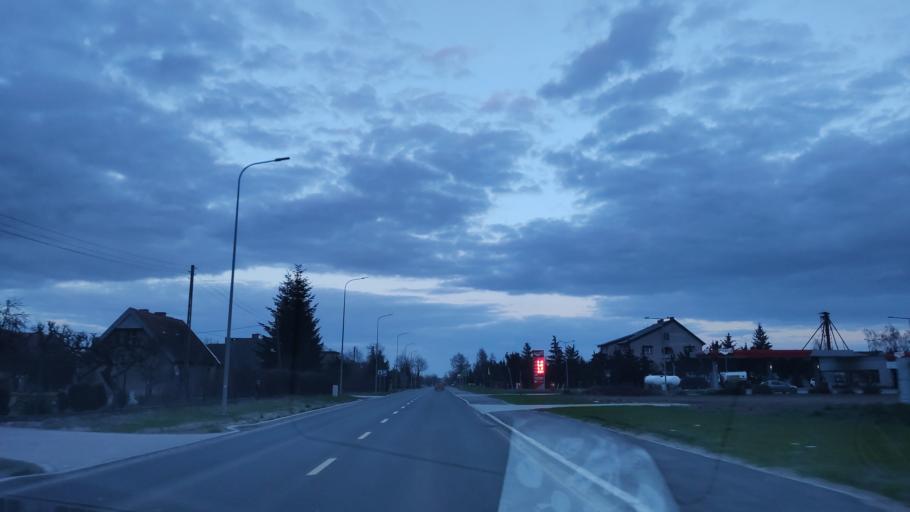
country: PL
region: Kujawsko-Pomorskie
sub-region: Powiat zninski
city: Znin
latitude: 52.8497
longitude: 17.7004
